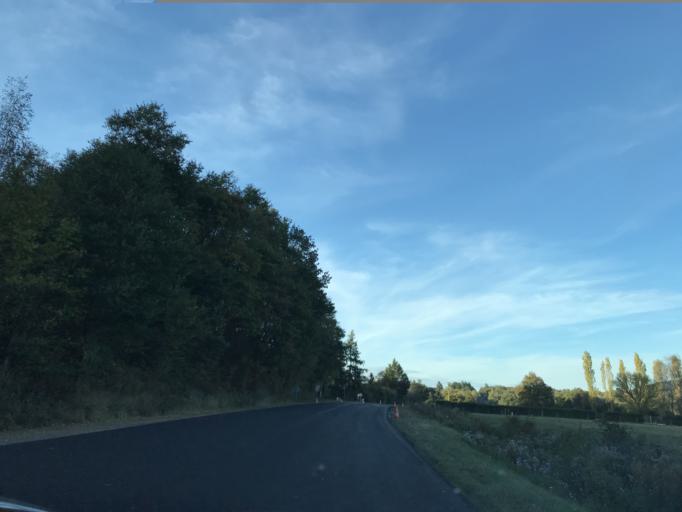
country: FR
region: Auvergne
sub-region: Departement du Puy-de-Dome
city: Paslieres
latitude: 45.8928
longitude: 3.5190
